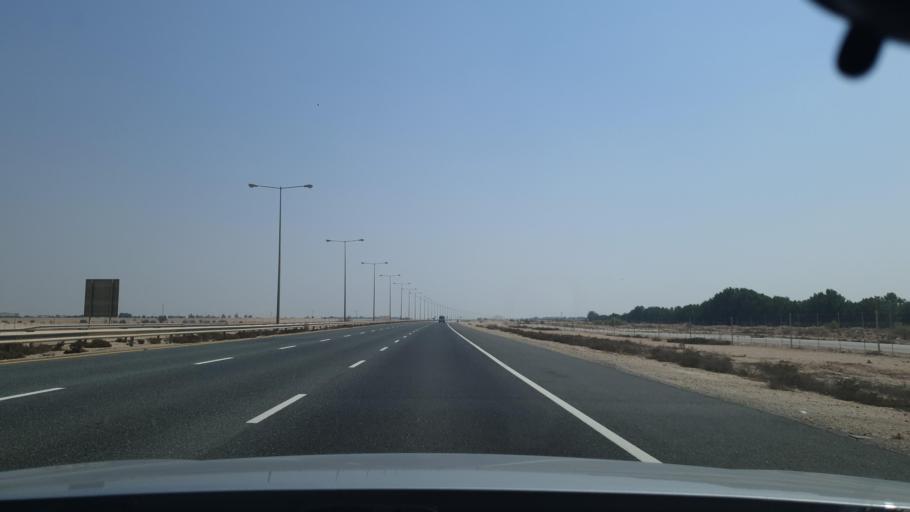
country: QA
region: Al Khawr
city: Al Khawr
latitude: 25.7803
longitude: 51.4032
